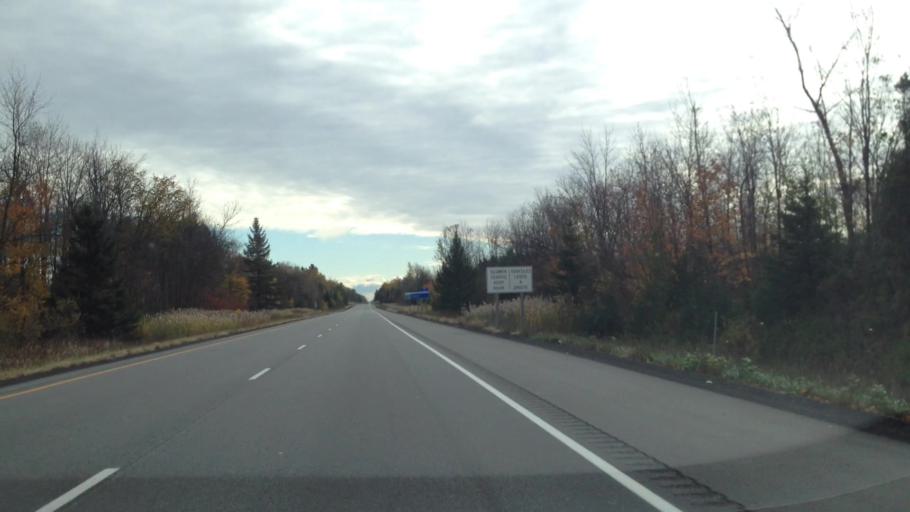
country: CA
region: Ontario
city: Hawkesbury
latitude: 45.5615
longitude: -74.4840
